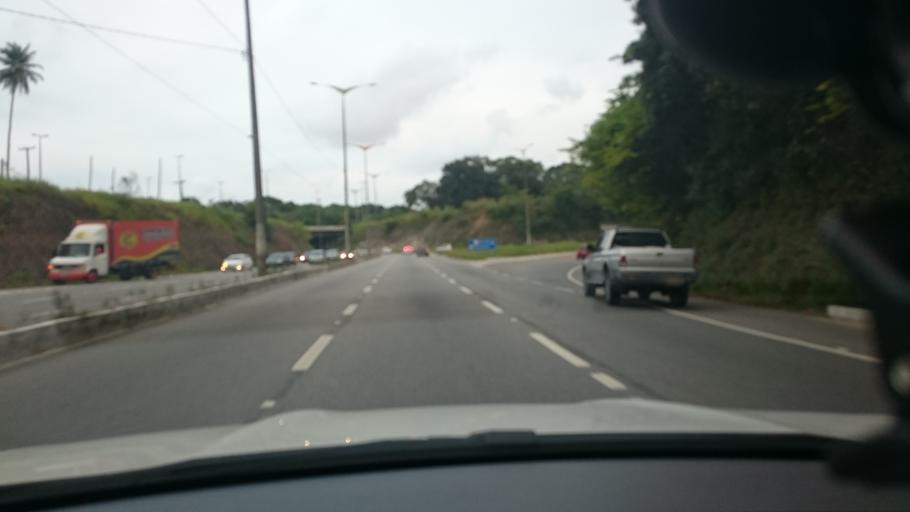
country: BR
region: Paraiba
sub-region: Joao Pessoa
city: Joao Pessoa
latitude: -7.1369
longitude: -34.8553
